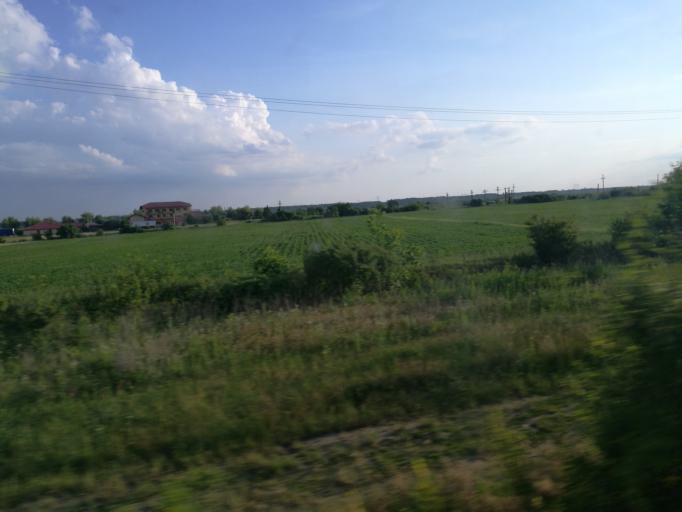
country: RO
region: Arges
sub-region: Comuna Calinesti
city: Calinesti
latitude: 44.8139
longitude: 25.0514
